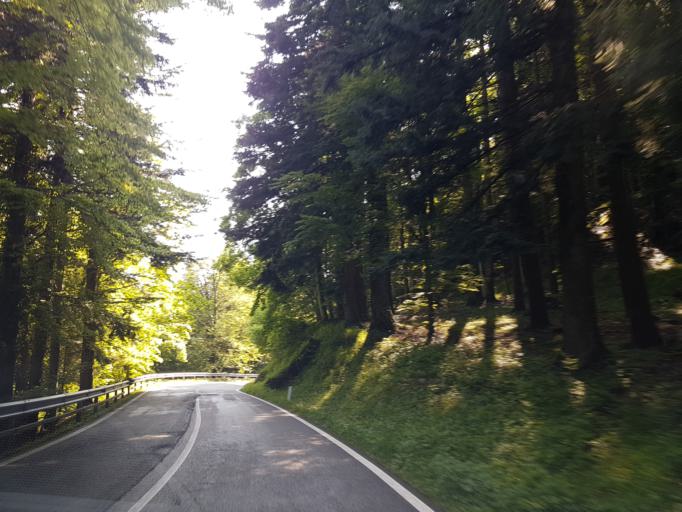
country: IT
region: Tuscany
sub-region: Province of Arezzo
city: Soci
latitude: 43.7957
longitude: 11.8884
